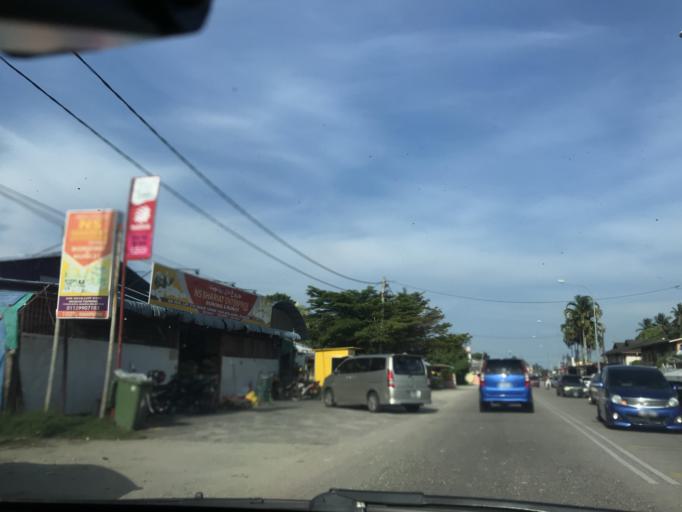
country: MY
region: Kelantan
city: Kota Bharu
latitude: 6.1239
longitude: 102.2784
